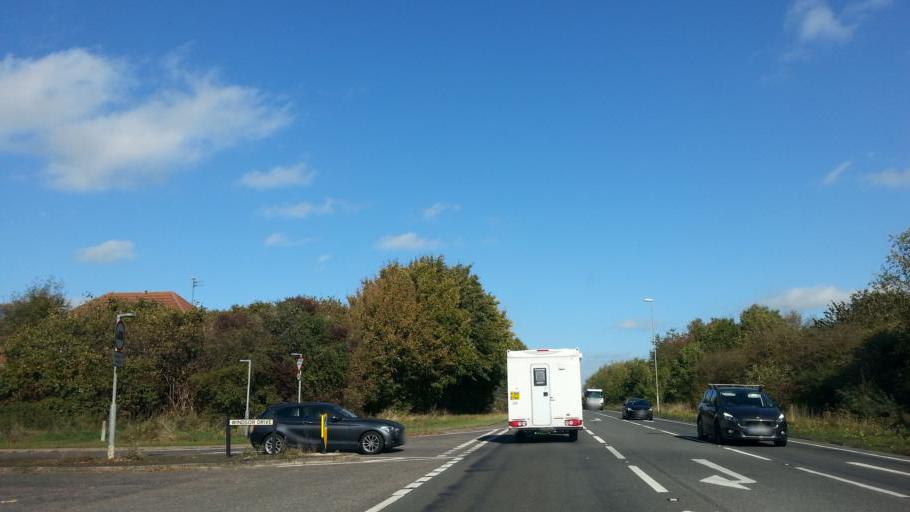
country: GB
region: England
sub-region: Northamptonshire
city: Thrapston
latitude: 52.3962
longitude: -0.5222
